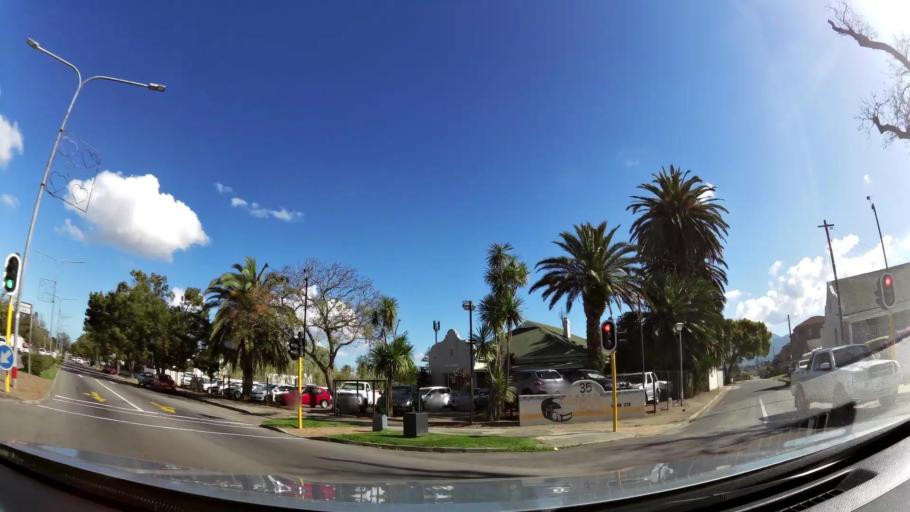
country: ZA
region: Western Cape
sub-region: Eden District Municipality
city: George
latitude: -33.9668
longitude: 22.4504
